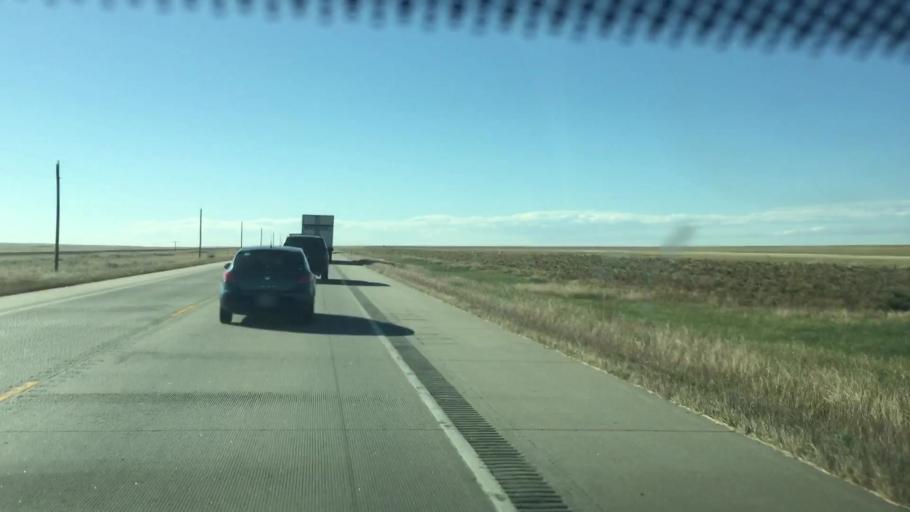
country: US
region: Colorado
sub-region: Kiowa County
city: Eads
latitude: 38.8332
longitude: -103.0563
